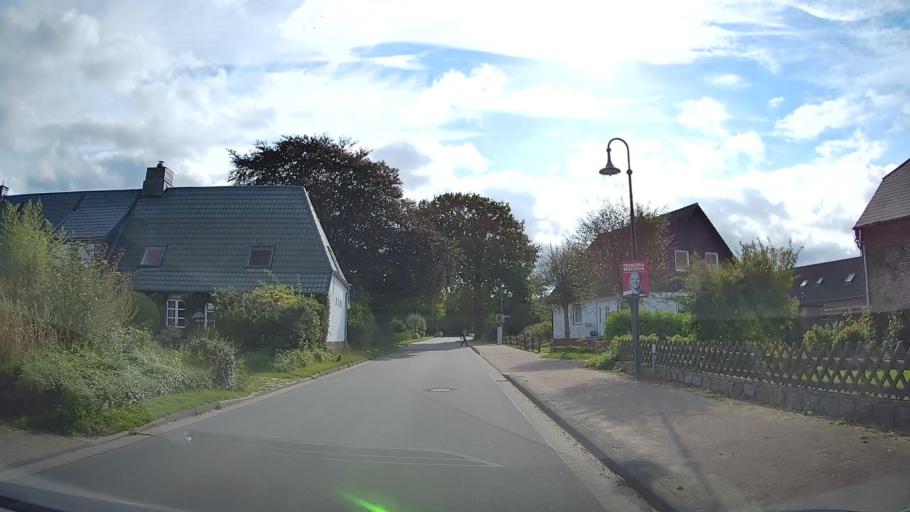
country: DE
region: Schleswig-Holstein
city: Ringsberg
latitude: 54.8059
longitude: 9.5986
